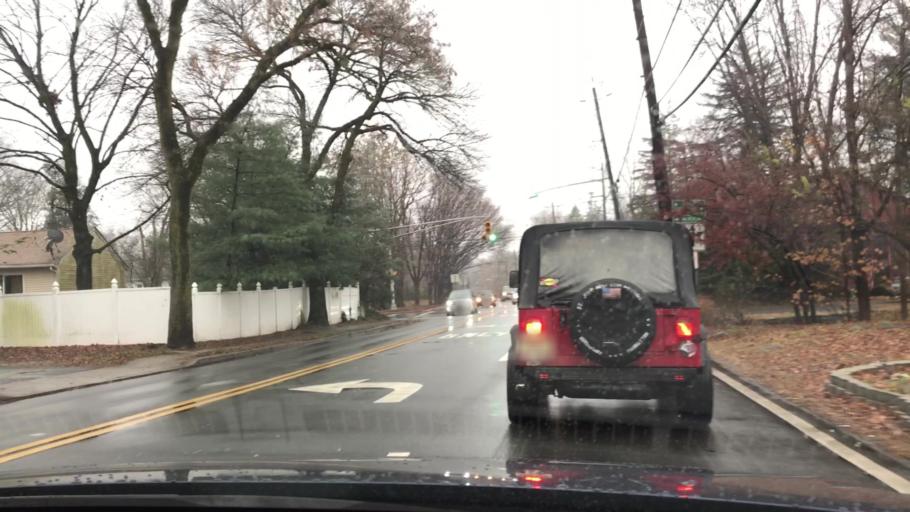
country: US
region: New Jersey
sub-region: Bergen County
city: Ho-Ho-Kus
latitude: 40.9804
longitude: -74.0880
